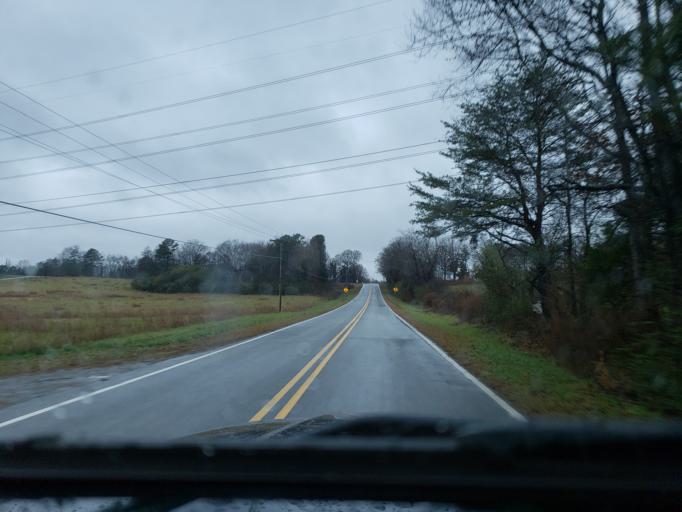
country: US
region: North Carolina
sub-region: Cleveland County
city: White Plains
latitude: 35.1854
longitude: -81.3783
